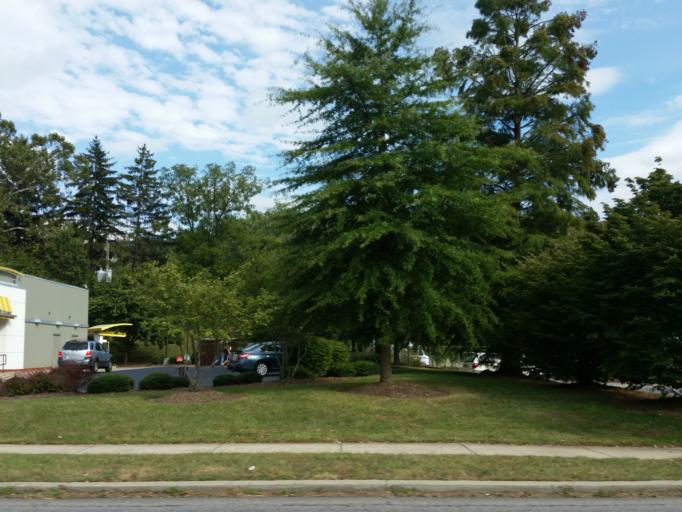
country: US
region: North Carolina
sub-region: Buncombe County
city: Asheville
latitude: 35.6242
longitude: -82.5545
